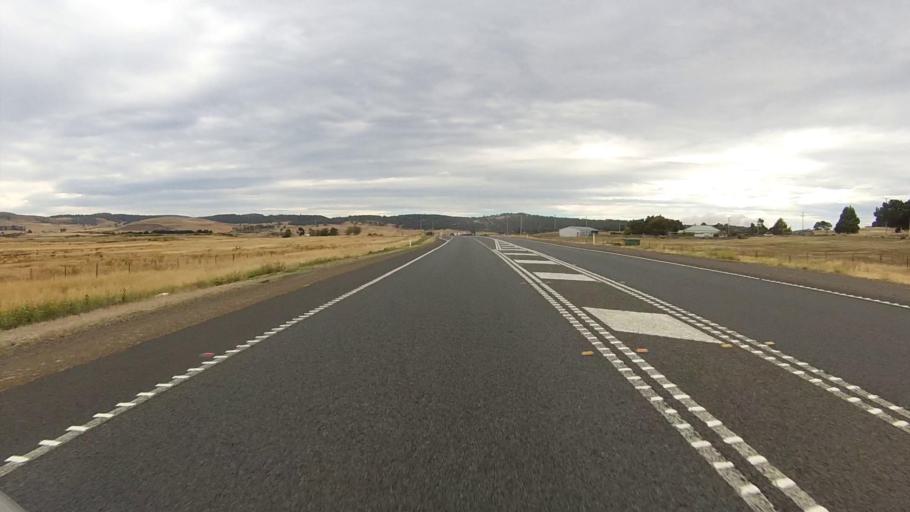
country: AU
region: Tasmania
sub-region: Brighton
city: Bridgewater
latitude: -42.3123
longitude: 147.3565
